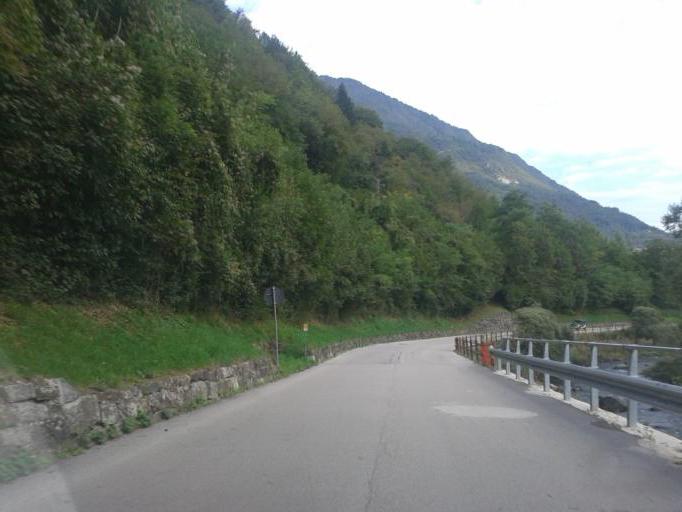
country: IT
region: Trentino-Alto Adige
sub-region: Provincia di Trento
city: Cimego
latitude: 45.9051
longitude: 10.6086
